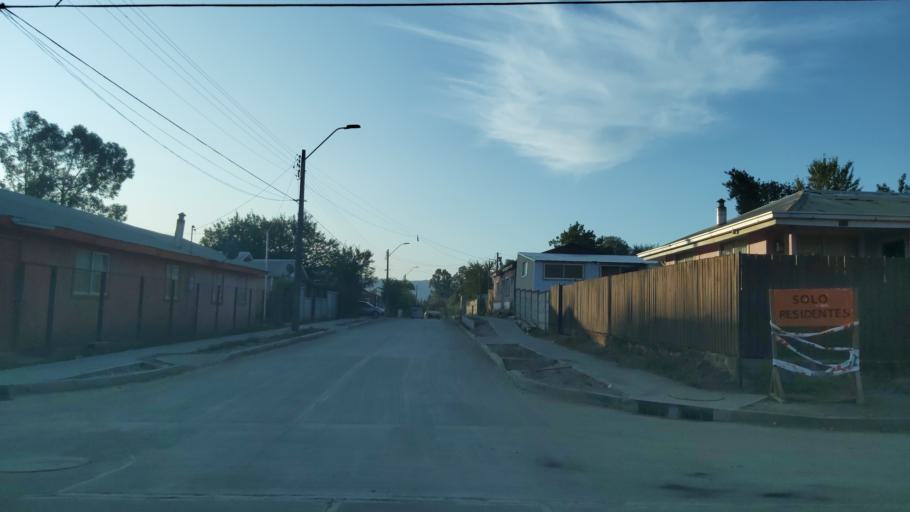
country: CL
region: Biobio
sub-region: Provincia de Biobio
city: La Laja
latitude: -37.1621
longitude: -72.9094
